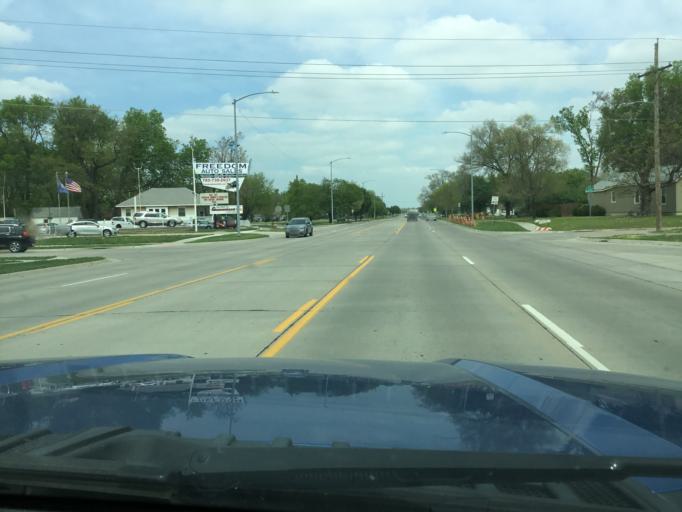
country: US
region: Kansas
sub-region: Shawnee County
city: Topeka
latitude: 39.0733
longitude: -95.6703
